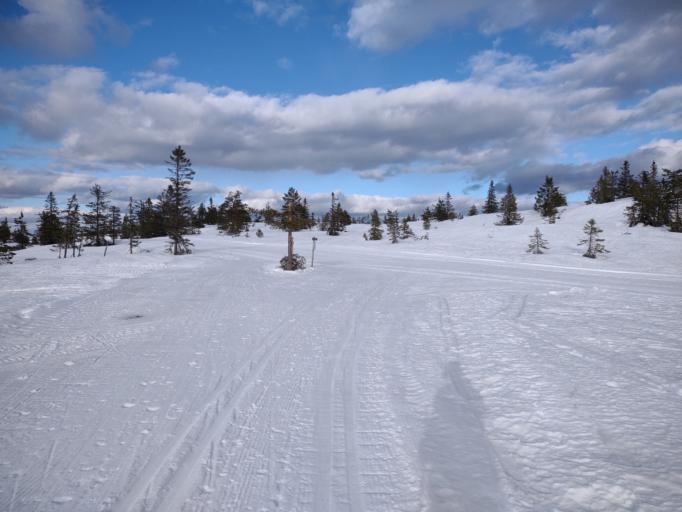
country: NO
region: Buskerud
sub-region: Flesberg
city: Lampeland
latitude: 59.7701
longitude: 9.4036
